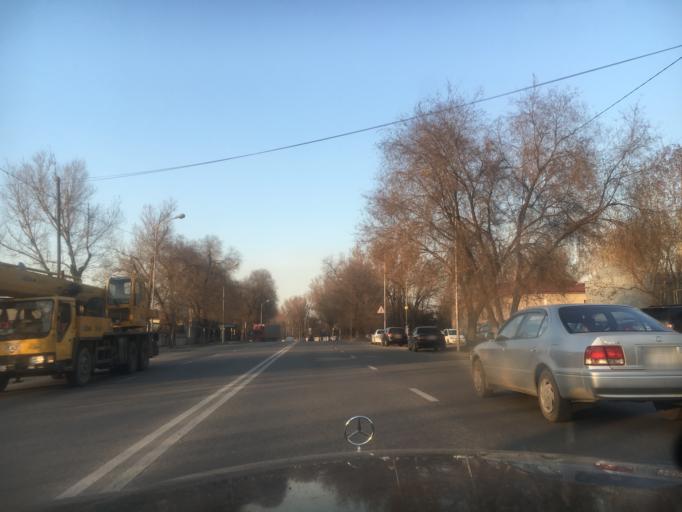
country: KZ
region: Almaty Oblysy
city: Pervomayskiy
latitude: 43.3651
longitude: 76.9850
